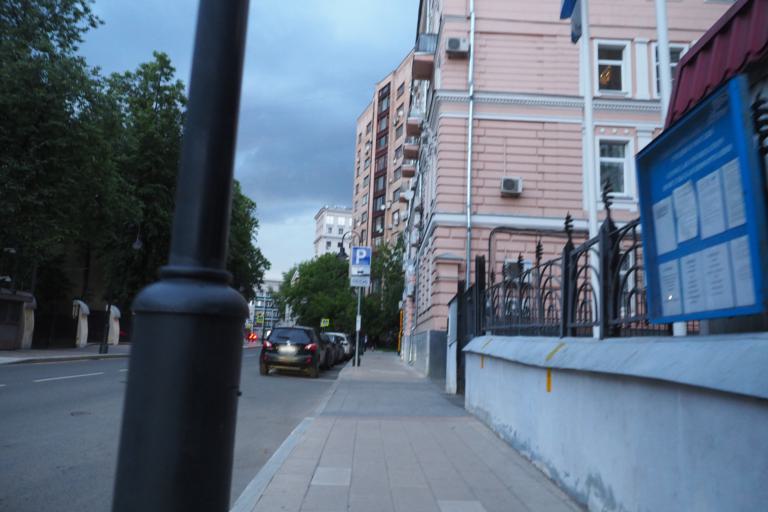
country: RU
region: Moscow
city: Moscow
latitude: 55.7601
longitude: 37.5939
